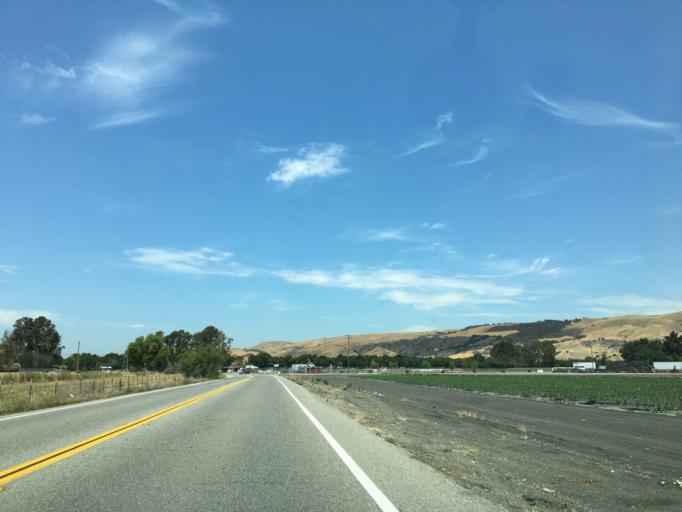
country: US
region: California
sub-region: Santa Clara County
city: Morgan Hill
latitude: 37.1979
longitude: -121.7350
